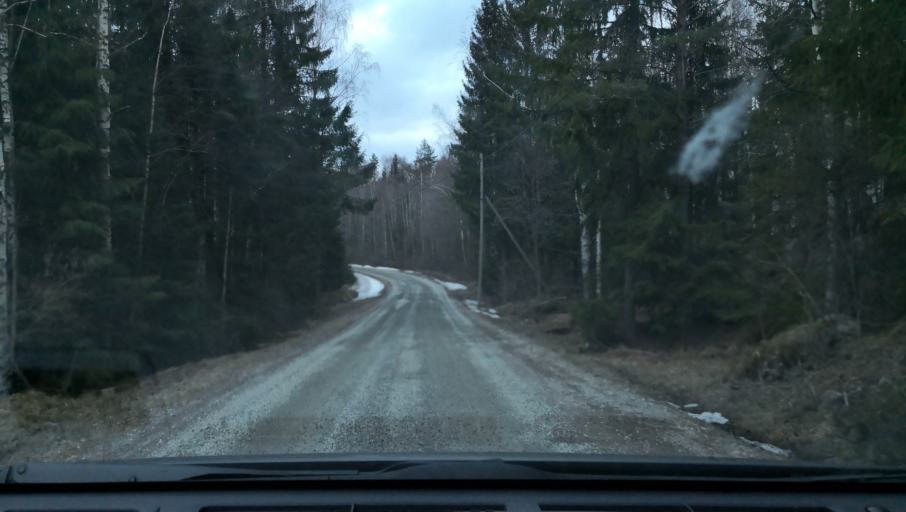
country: SE
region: Vaestmanland
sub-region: Kopings Kommun
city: Kolsva
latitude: 59.6020
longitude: 15.6546
